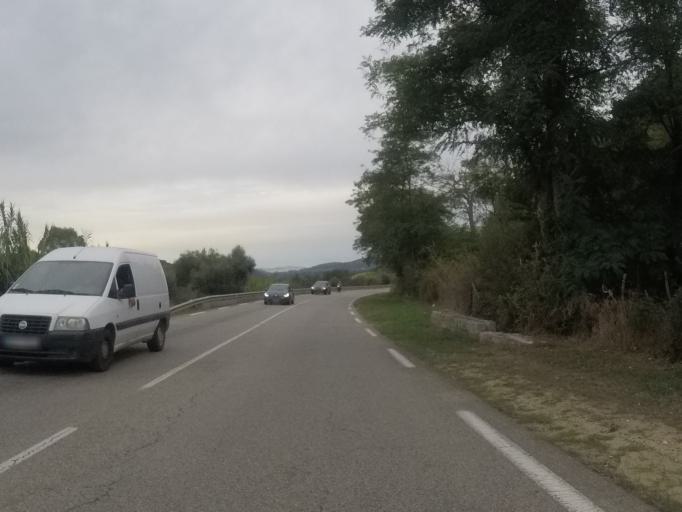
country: FR
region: Corsica
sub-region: Departement de la Corse-du-Sud
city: Sarrola-Carcopino
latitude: 41.9834
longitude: 8.8405
